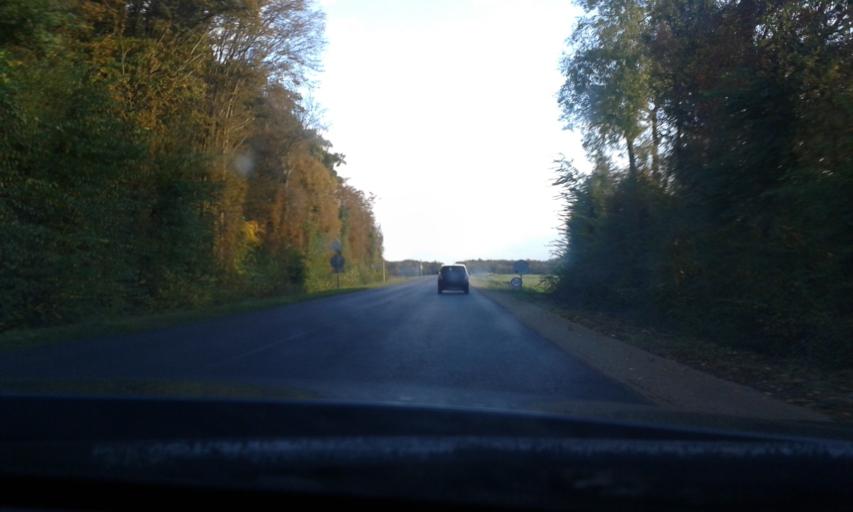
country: FR
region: Centre
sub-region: Departement d'Eure-et-Loir
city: Sours
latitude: 48.4024
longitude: 1.5520
